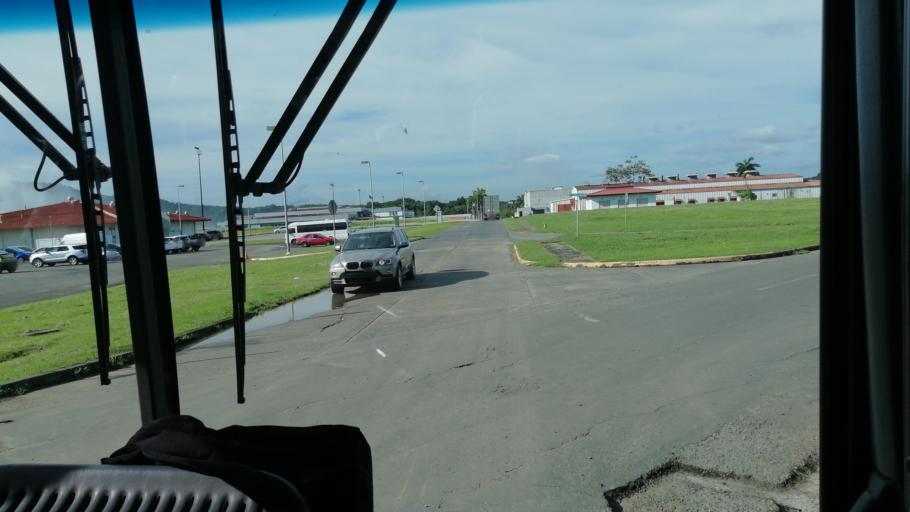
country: PA
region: Panama
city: Veracruz
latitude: 8.9172
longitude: -79.5944
